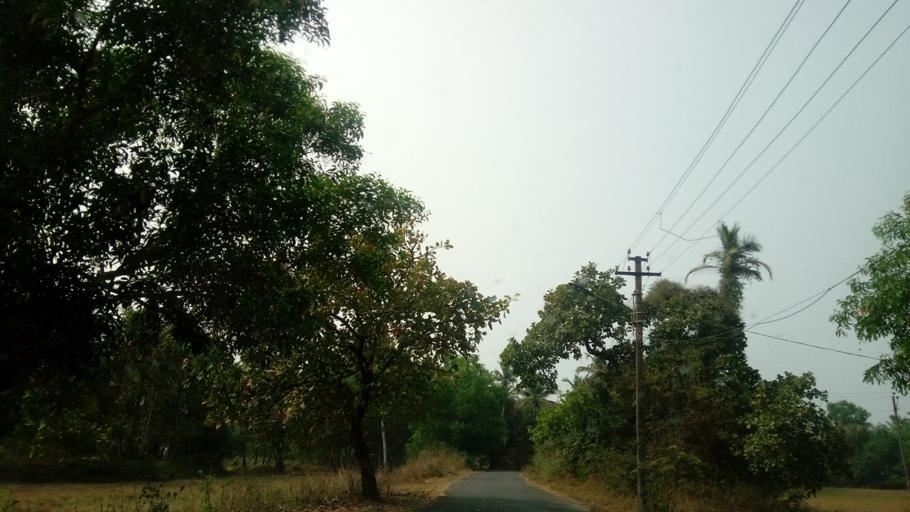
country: IN
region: Goa
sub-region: South Goa
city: Varca
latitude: 15.2206
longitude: 73.9393
